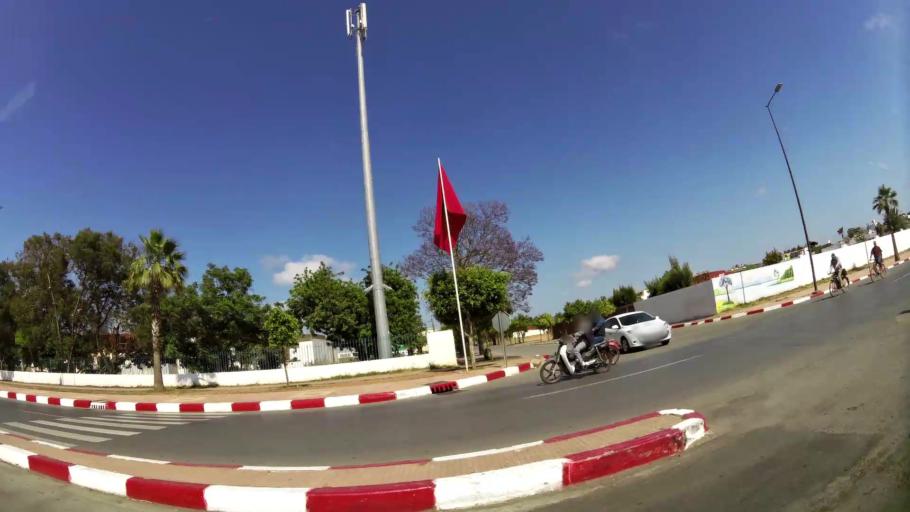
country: MA
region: Rabat-Sale-Zemmour-Zaer
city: Sale
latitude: 34.0398
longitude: -6.7751
